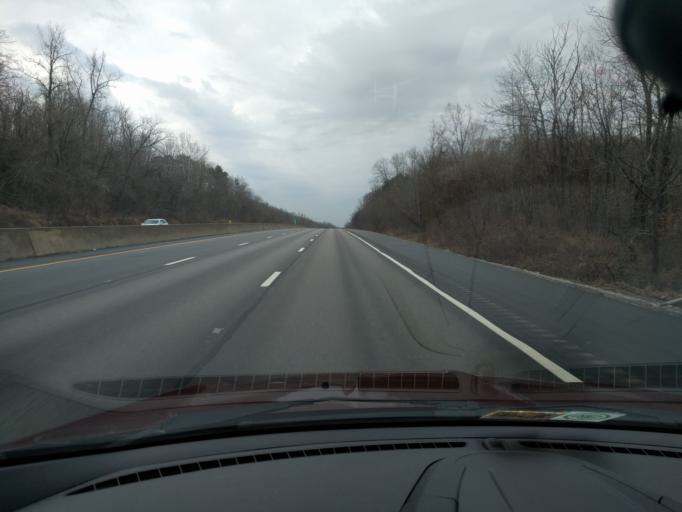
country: US
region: West Virginia
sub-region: Wood County
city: Parkersburg
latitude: 39.2542
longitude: -81.5004
